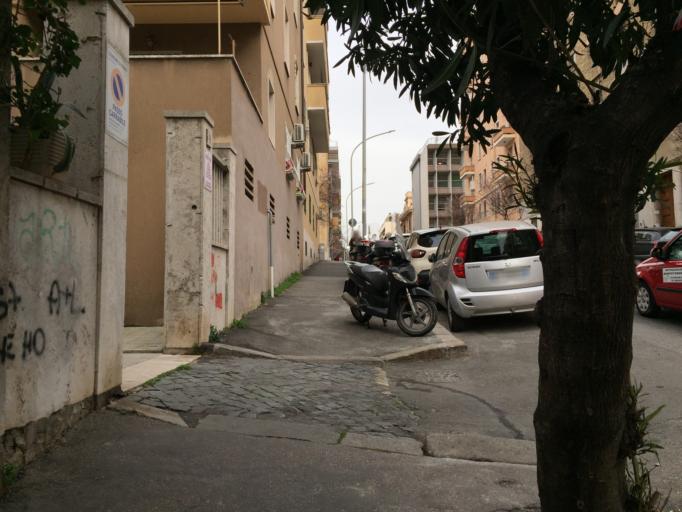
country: VA
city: Vatican City
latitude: 41.8827
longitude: 12.4598
